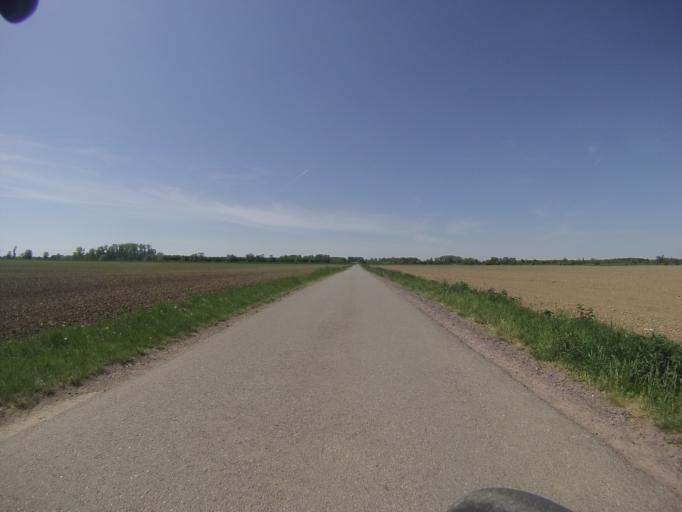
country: CZ
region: South Moravian
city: Novosedly
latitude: 48.8156
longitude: 16.4754
